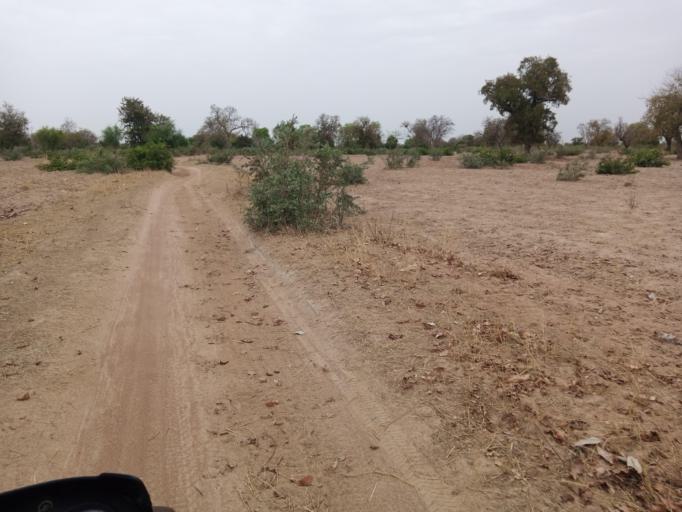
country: BF
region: Boucle du Mouhoun
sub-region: Province de la Kossi
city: Nouna
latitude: 12.8299
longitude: -4.0773
